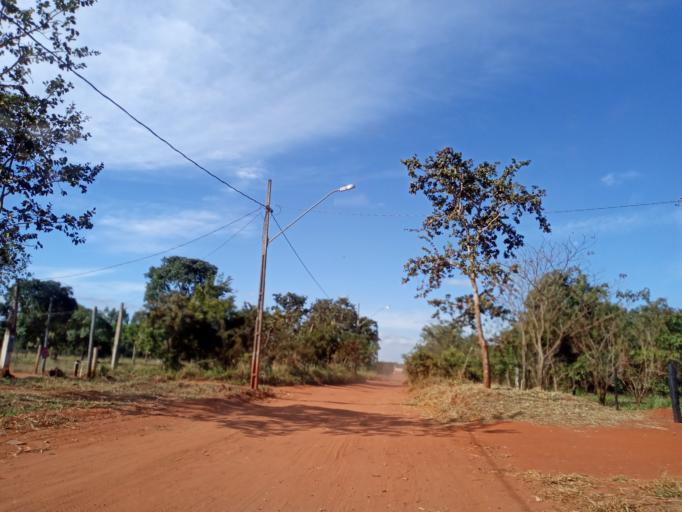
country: BR
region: Minas Gerais
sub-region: Ituiutaba
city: Ituiutaba
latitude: -18.9556
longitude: -49.4846
